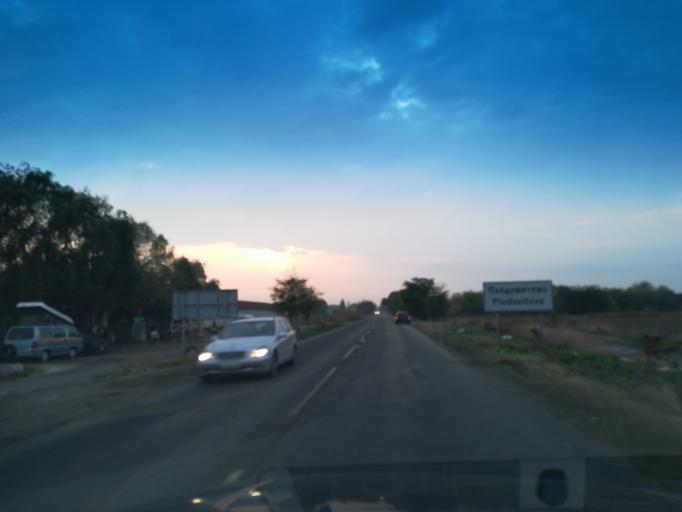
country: BG
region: Stara Zagora
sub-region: Obshtina Chirpan
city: Chirpan
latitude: 42.1784
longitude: 25.2165
